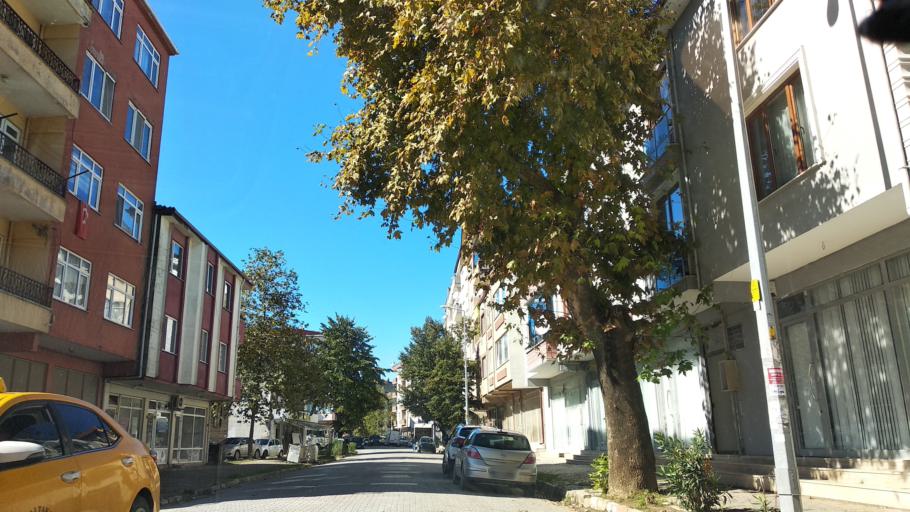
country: TR
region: Sakarya
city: Karasu
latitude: 41.0923
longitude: 30.6952
